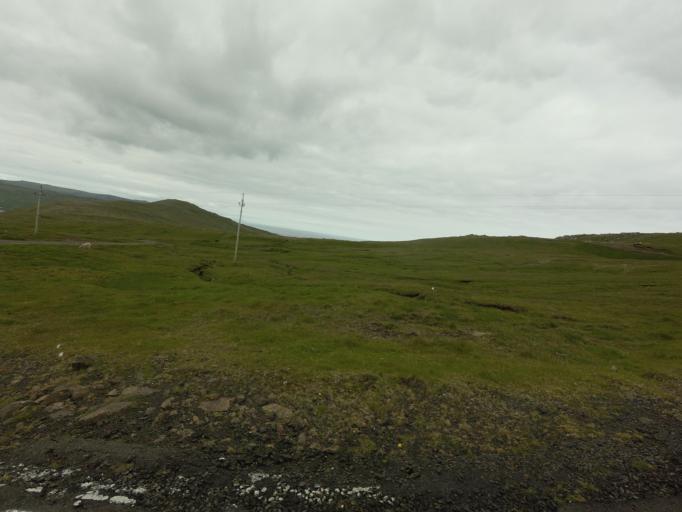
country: FO
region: Suduroy
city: Vagur
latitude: 61.4277
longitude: -6.7565
